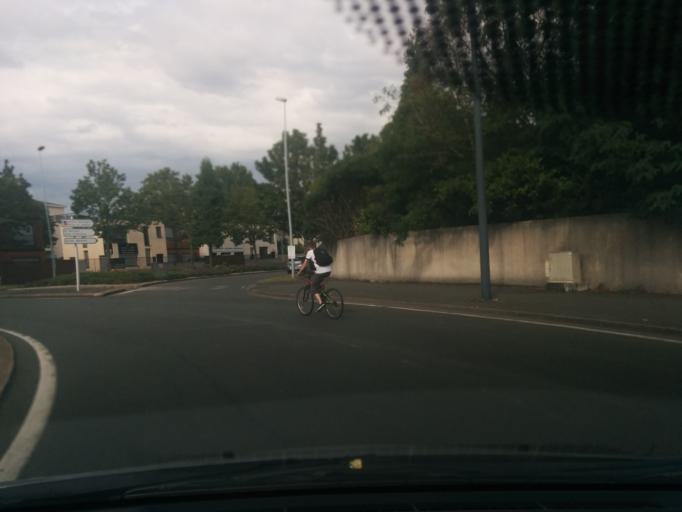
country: FR
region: Pays de la Loire
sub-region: Departement de Maine-et-Loire
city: Angers
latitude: 47.4482
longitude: -0.5382
